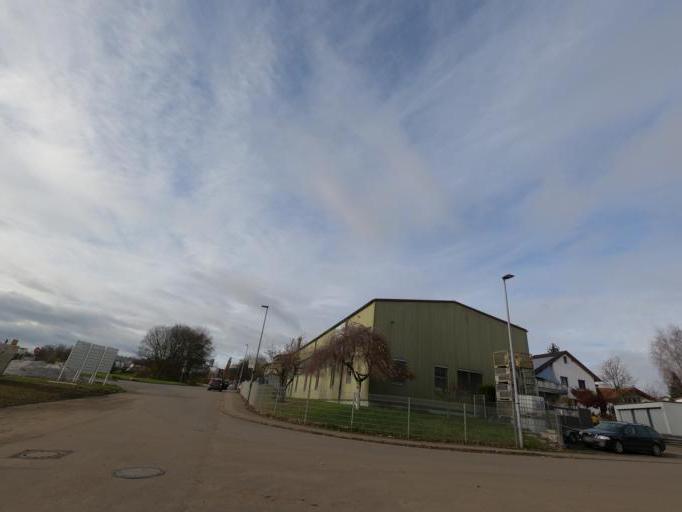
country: DE
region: Baden-Wuerttemberg
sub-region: Regierungsbezirk Stuttgart
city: Albershausen
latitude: 48.6870
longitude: 9.5558
